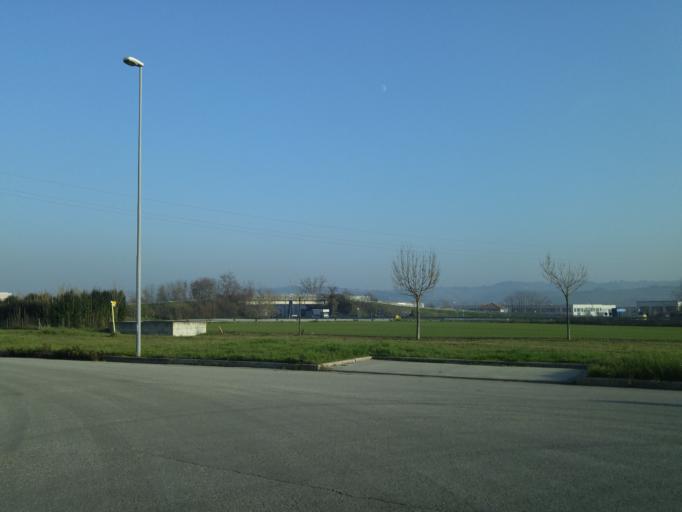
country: IT
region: The Marches
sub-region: Provincia di Pesaro e Urbino
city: Lucrezia
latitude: 43.7694
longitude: 12.9554
